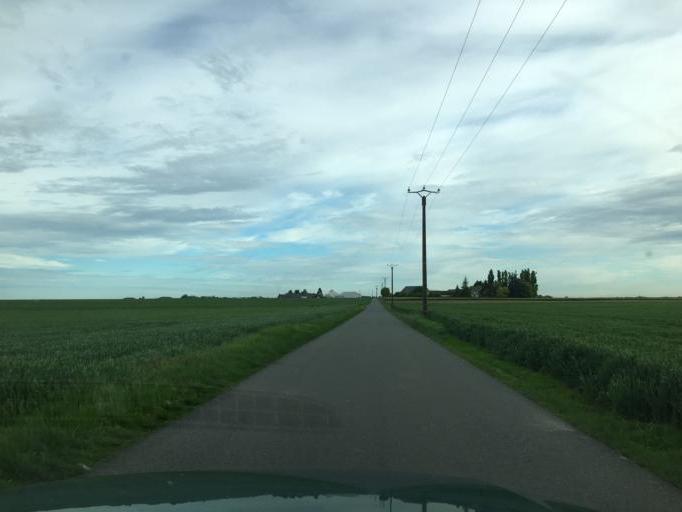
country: FR
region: Centre
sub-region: Departement du Loiret
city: Bricy
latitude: 47.9698
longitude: 1.7482
